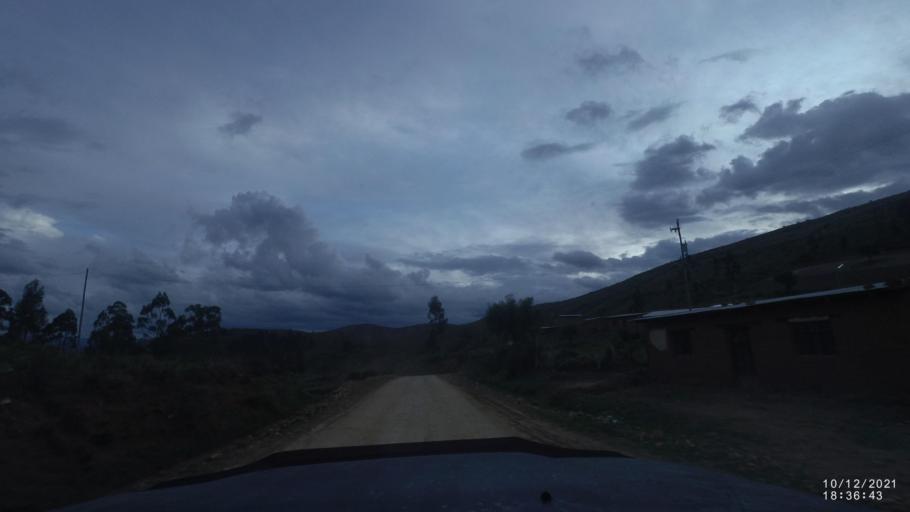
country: BO
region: Cochabamba
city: Tarata
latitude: -17.8336
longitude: -65.9916
